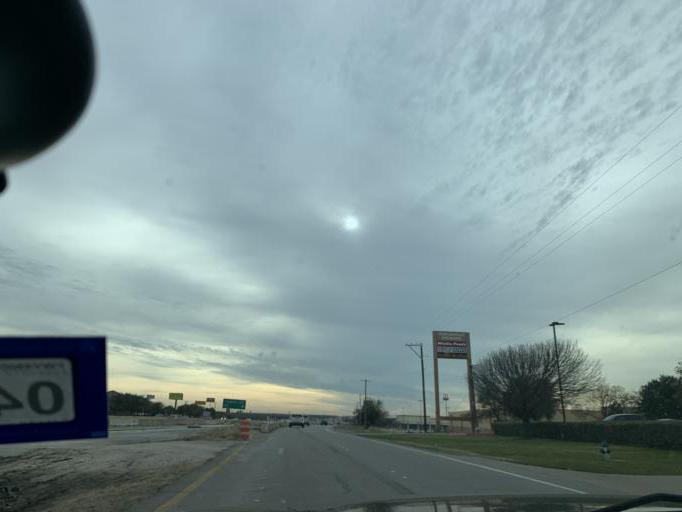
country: US
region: Texas
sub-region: Dallas County
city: Duncanville
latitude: 32.6460
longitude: -96.8869
